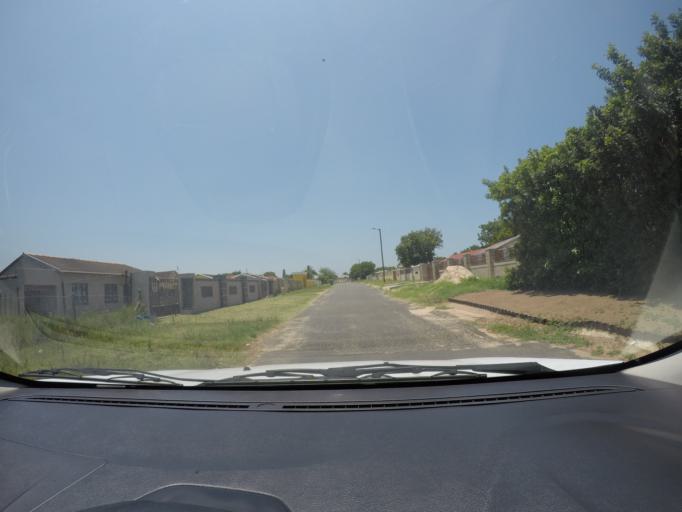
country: ZA
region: KwaZulu-Natal
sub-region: uThungulu District Municipality
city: eSikhawini
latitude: -28.8852
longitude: 31.8962
